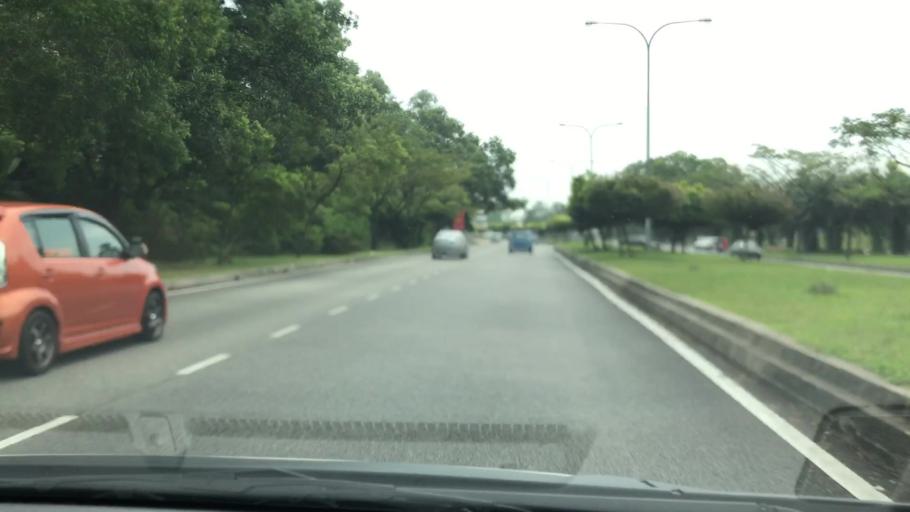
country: MY
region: Putrajaya
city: Putrajaya
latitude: 2.9954
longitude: 101.6642
